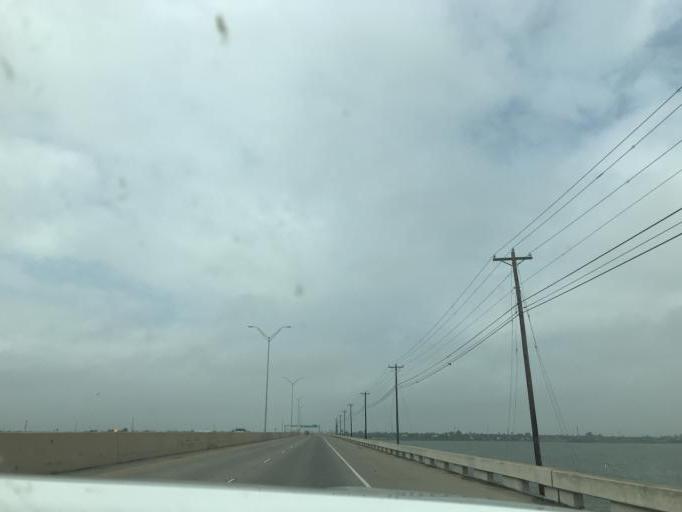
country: US
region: Texas
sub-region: Nueces County
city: Corpus Christi
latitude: 27.6607
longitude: -97.2666
